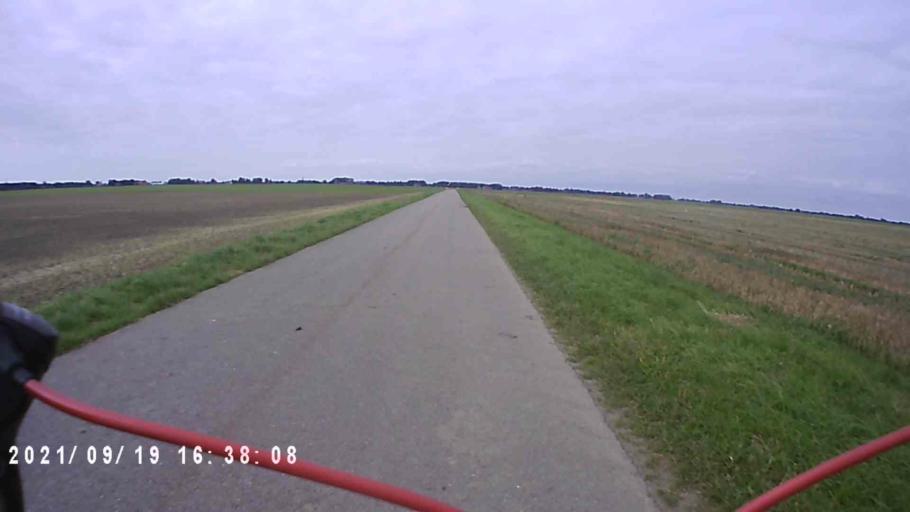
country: NL
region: Groningen
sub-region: Gemeente  Oldambt
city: Winschoten
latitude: 53.1867
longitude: 7.1331
